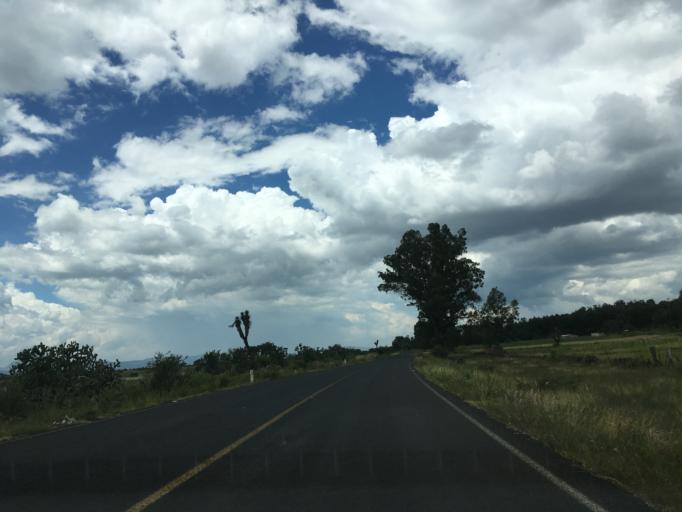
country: MX
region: Michoacan
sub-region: Zacapu
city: Naranja de Tapia
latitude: 19.8085
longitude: -101.6754
